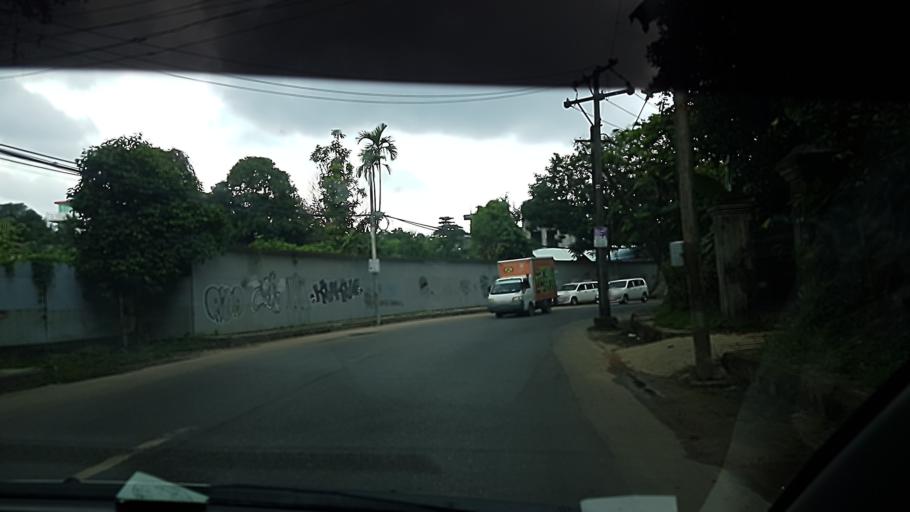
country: MM
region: Yangon
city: Yangon
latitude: 16.8013
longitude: 96.1685
